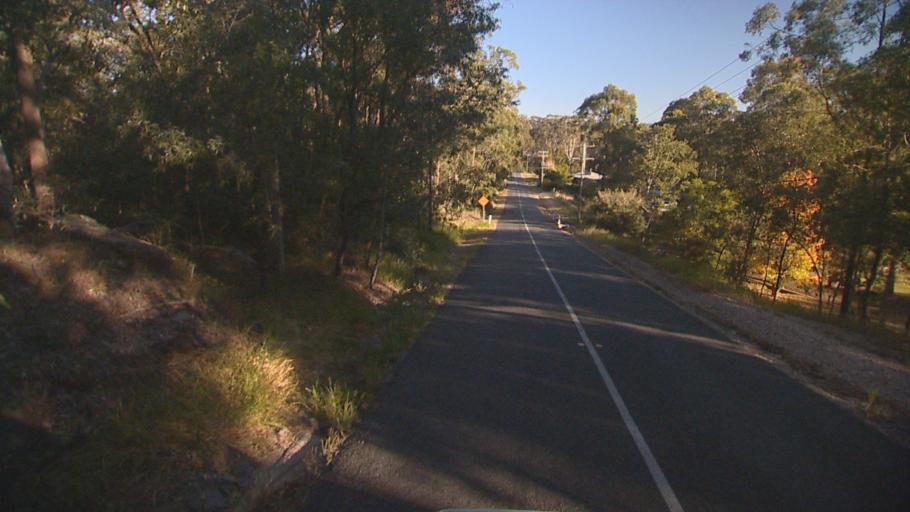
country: AU
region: Queensland
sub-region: Logan
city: Chambers Flat
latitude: -27.7652
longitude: 153.1226
